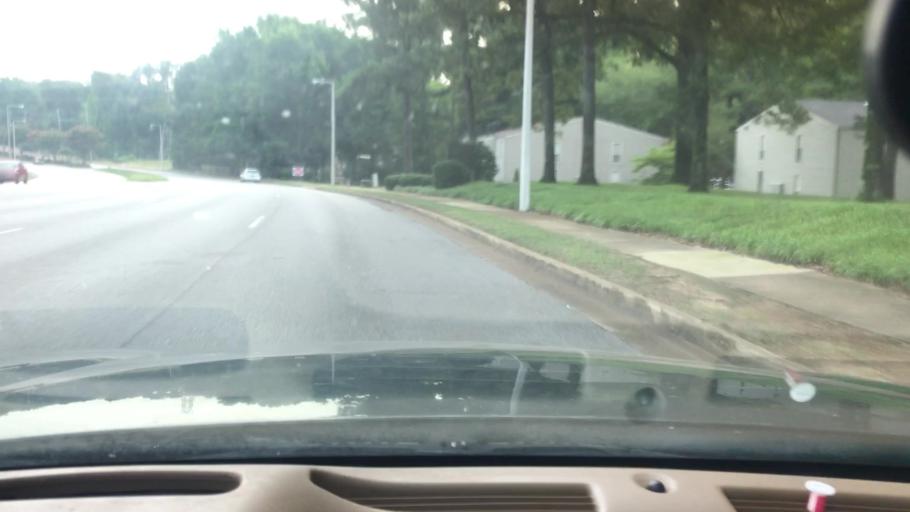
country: US
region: Tennessee
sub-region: Shelby County
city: Bartlett
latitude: 35.1857
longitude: -89.8699
